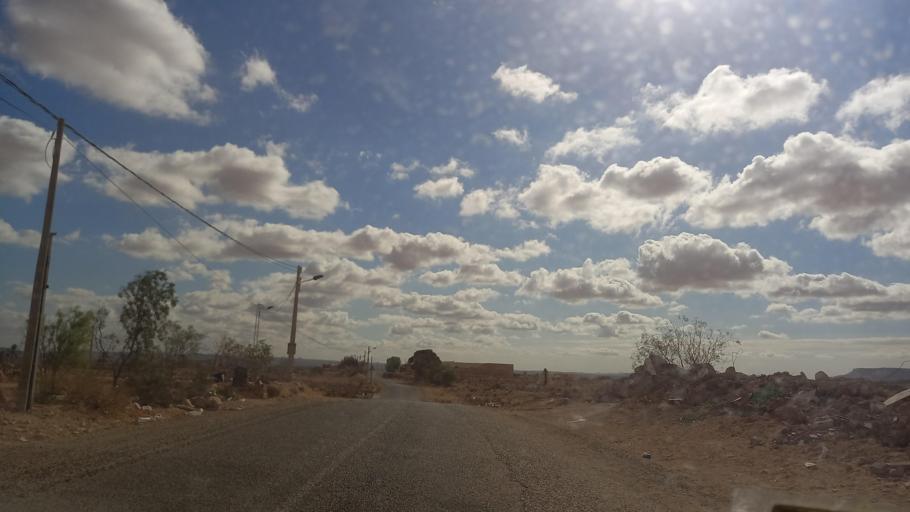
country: TN
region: Tataouine
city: Tataouine
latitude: 32.9800
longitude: 10.2696
